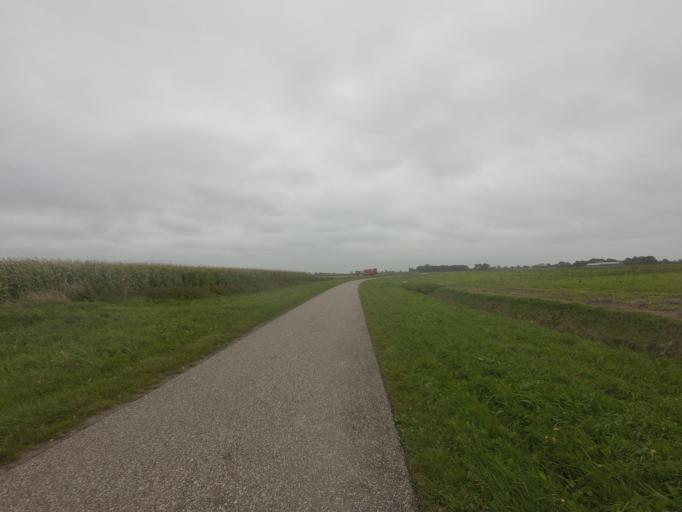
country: NL
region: Friesland
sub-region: Gemeente Ferwerderadiel
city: Ferwert
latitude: 53.3455
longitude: 5.8574
